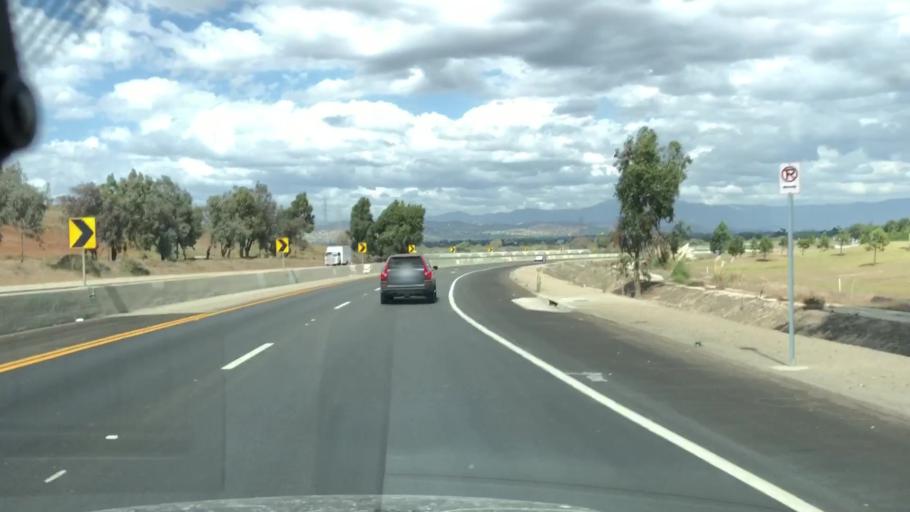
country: US
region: California
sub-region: Ventura County
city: Oxnard Shores
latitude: 34.2267
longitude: -119.2209
